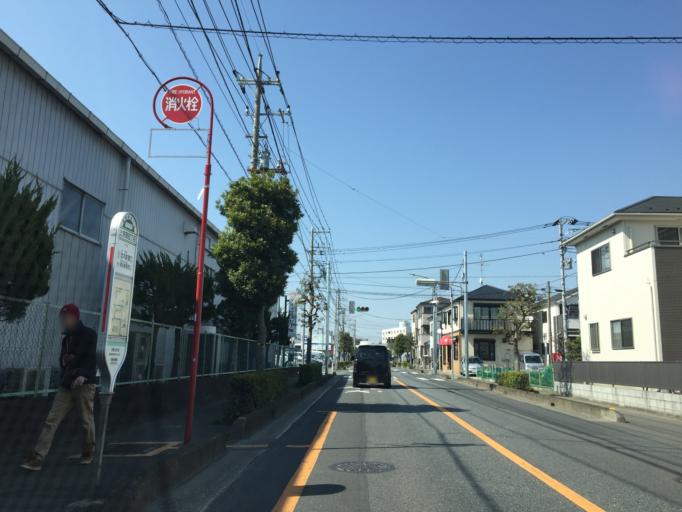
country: JP
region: Saitama
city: Shiki
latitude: 35.8478
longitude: 139.5886
